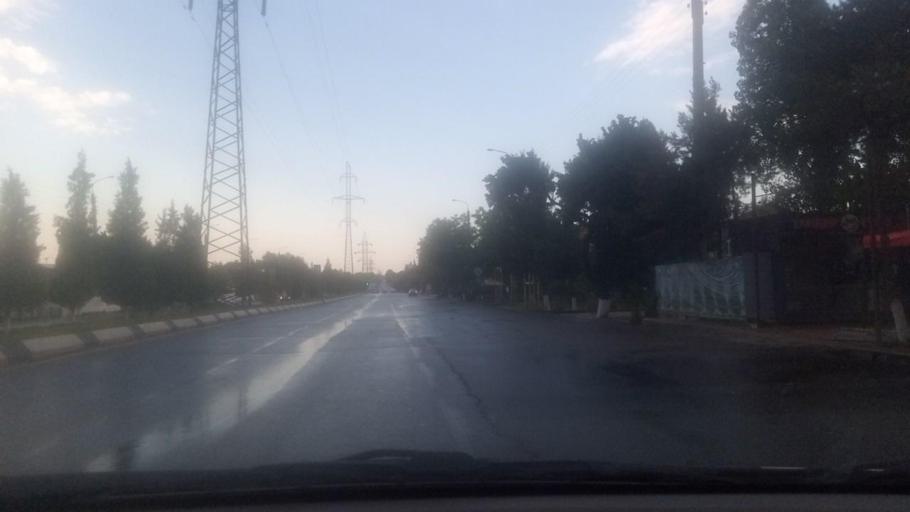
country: UZ
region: Toshkent Shahri
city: Tashkent
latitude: 41.3109
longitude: 69.1934
